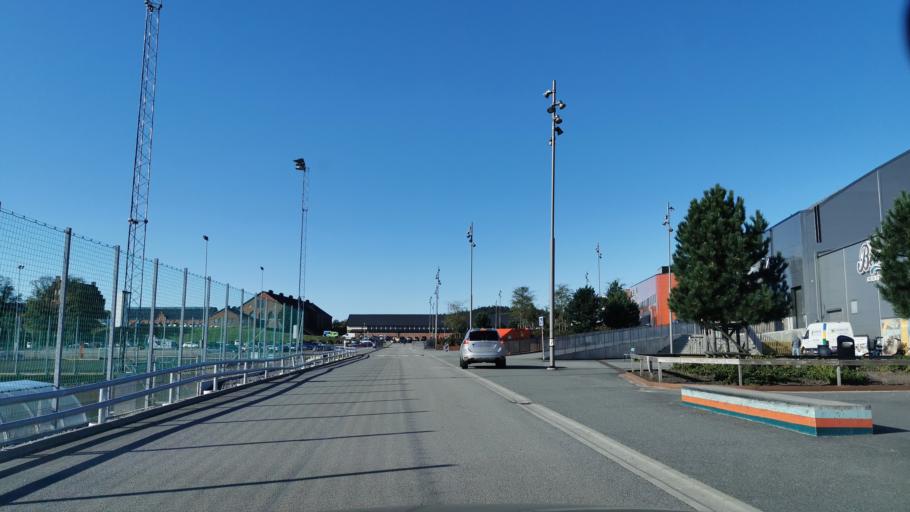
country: SE
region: Vaestra Goetaland
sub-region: Goteborg
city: Eriksbo
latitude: 57.7378
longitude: 12.0369
